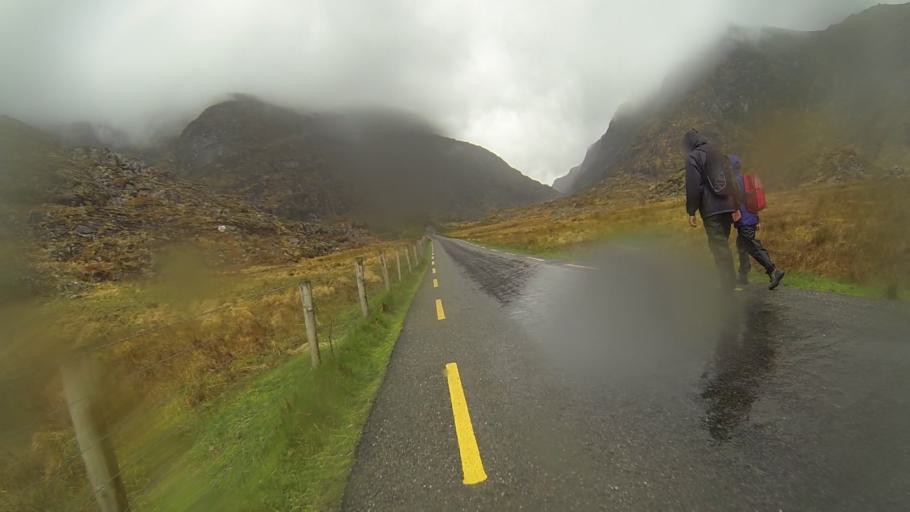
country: IE
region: Munster
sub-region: Ciarrai
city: Cill Airne
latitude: 52.0192
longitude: -9.6359
